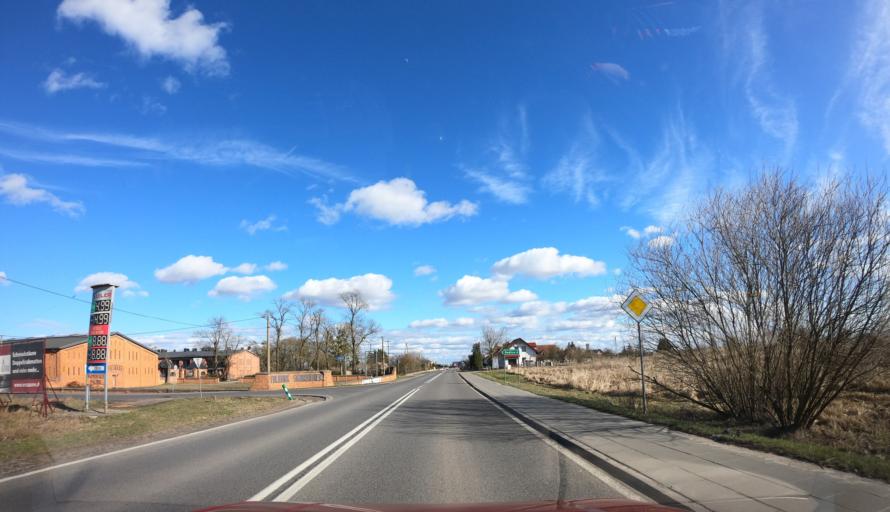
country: PL
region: West Pomeranian Voivodeship
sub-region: Powiat policki
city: Dobra
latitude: 53.4358
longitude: 14.4241
